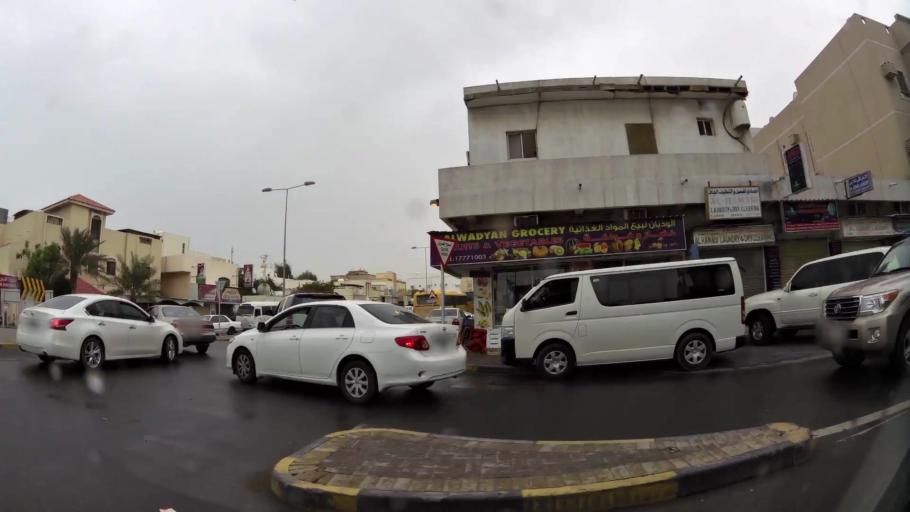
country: BH
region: Northern
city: Ar Rifa'
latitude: 26.1266
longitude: 50.5736
